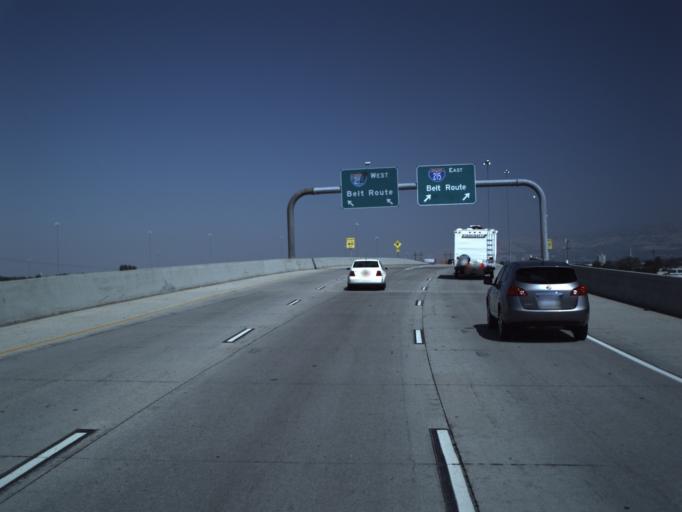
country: US
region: Utah
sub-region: Salt Lake County
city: Midvale
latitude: 40.6297
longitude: -111.9023
